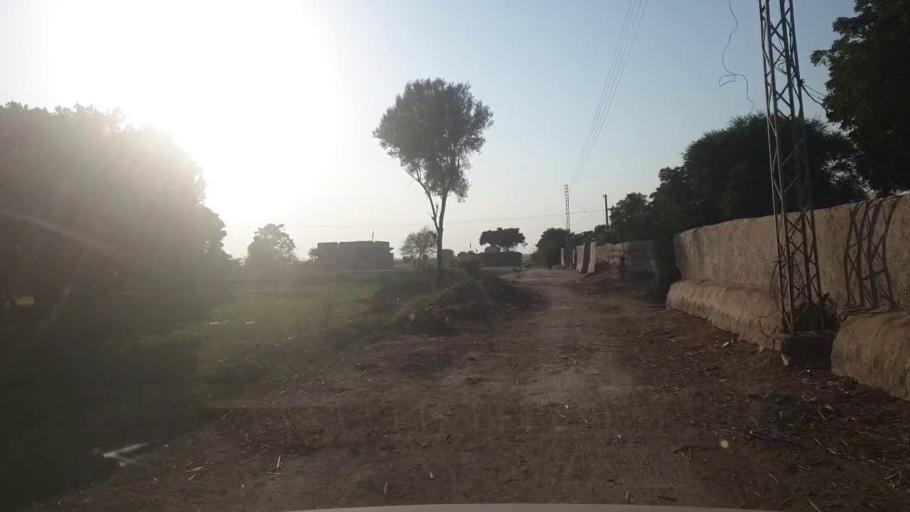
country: PK
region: Sindh
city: Chambar
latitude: 25.2766
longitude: 68.8784
